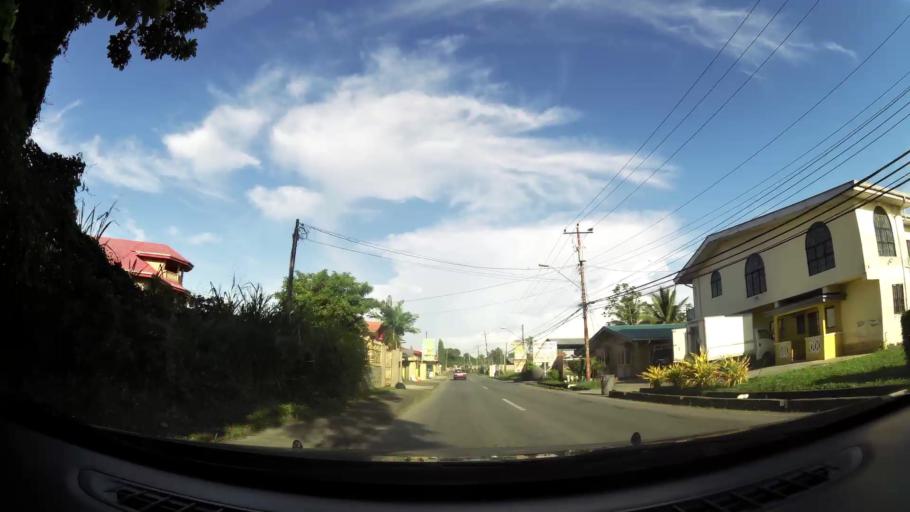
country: TT
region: Chaguanas
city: Chaguanas
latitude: 10.5514
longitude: -61.3616
